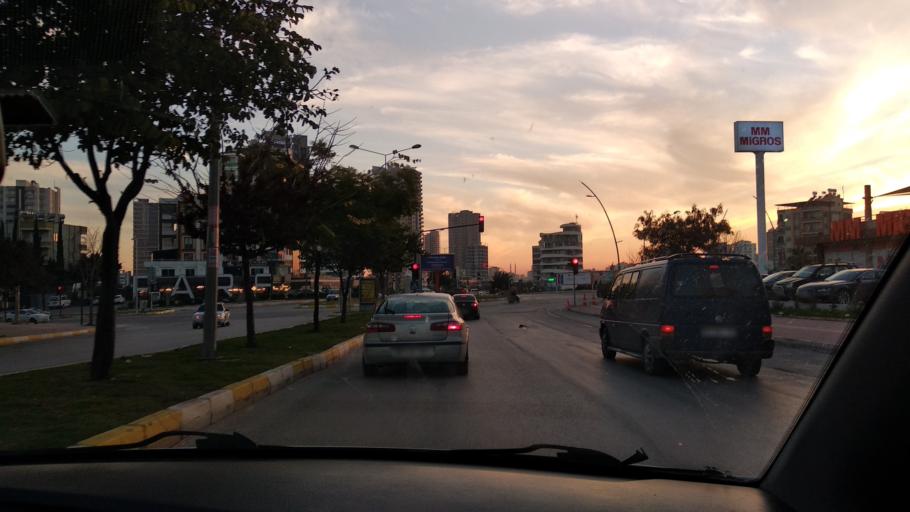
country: TR
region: Mersin
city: Mercin
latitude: 36.8038
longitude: 34.5853
